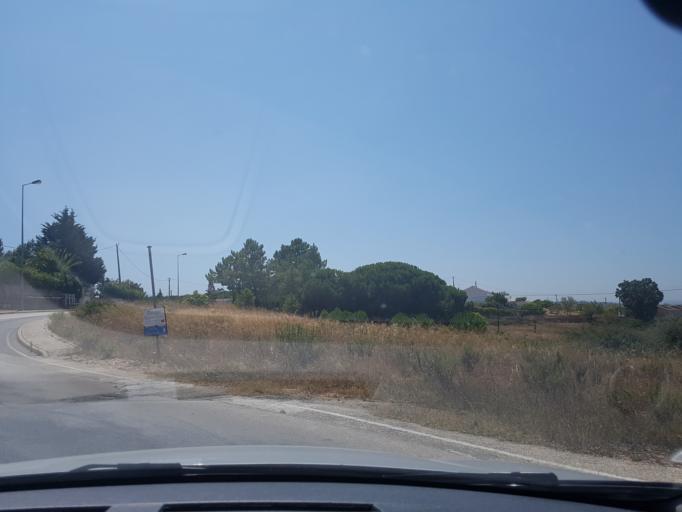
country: PT
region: Faro
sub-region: Lagoa
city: Carvoeiro
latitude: 37.1070
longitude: -8.4338
